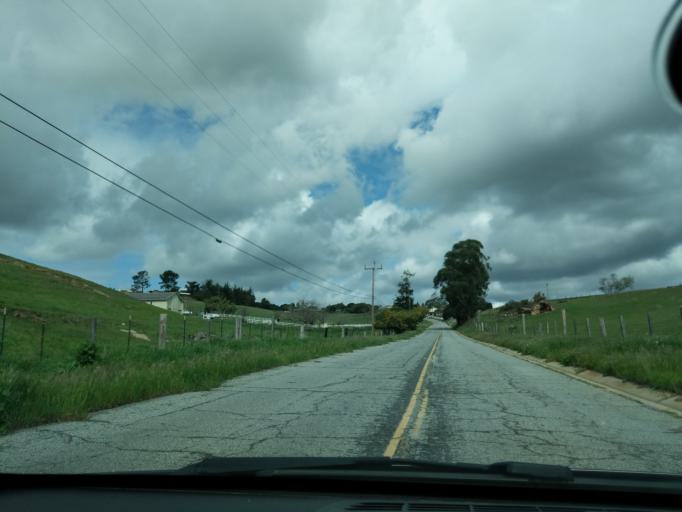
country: US
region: California
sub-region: Monterey County
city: Prunedale
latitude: 36.7573
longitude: -121.6569
